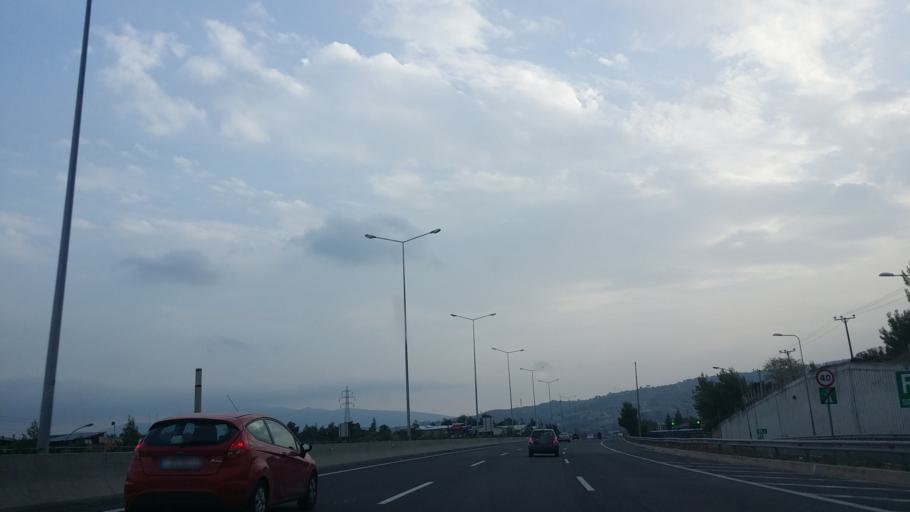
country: GR
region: Attica
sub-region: Nomarchia Anatolikis Attikis
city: Afidnes
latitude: 38.2046
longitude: 23.8548
